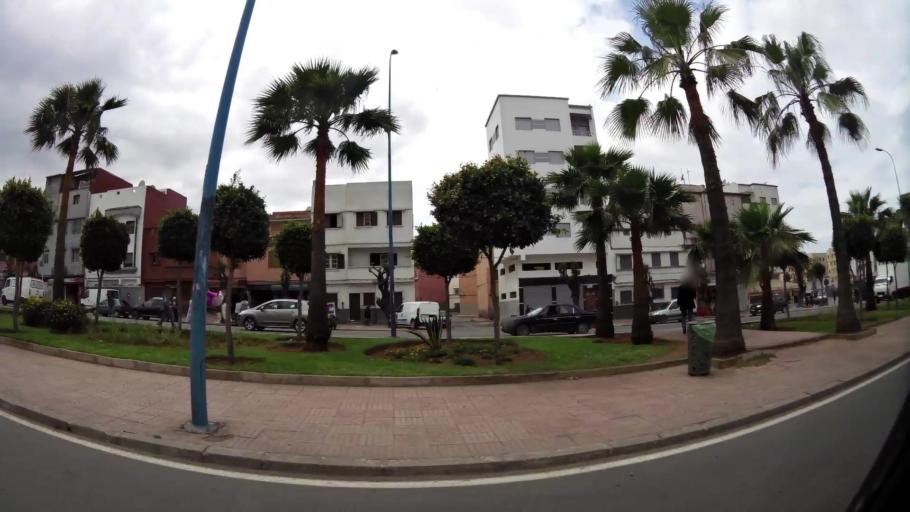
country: MA
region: Grand Casablanca
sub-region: Casablanca
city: Casablanca
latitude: 33.5684
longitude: -7.5589
